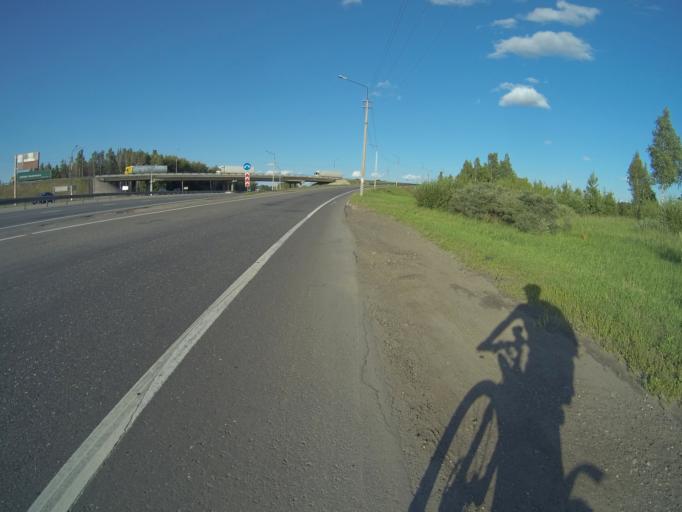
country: RU
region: Vladimir
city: Vorsha
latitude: 56.0799
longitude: 40.1961
